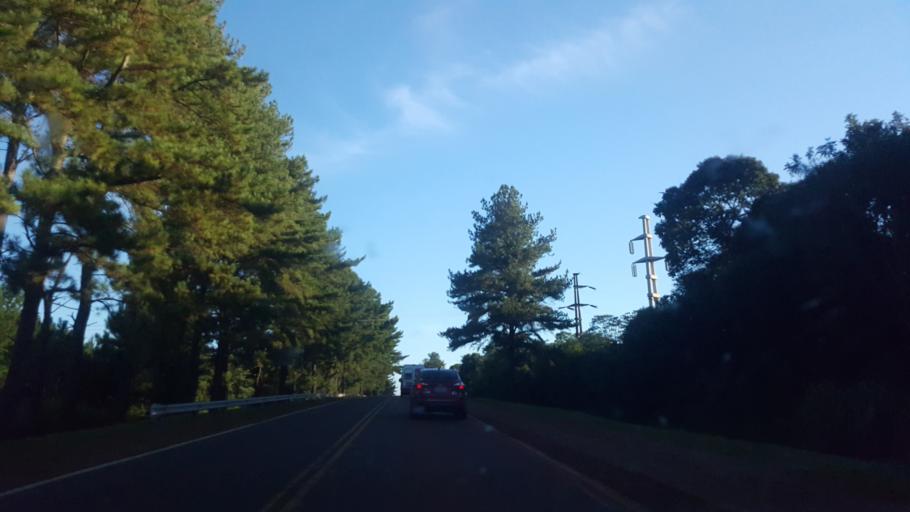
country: AR
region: Misiones
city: El Alcazar
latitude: -26.7489
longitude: -54.8836
